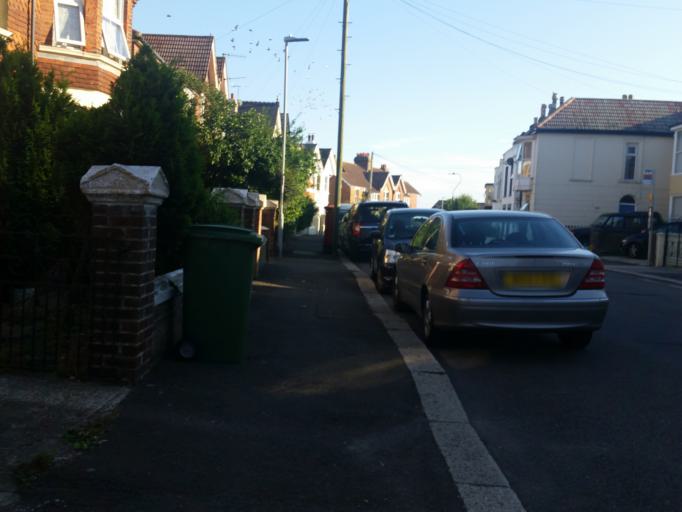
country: GB
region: England
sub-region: East Sussex
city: Hastings
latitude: 50.8613
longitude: 0.5896
